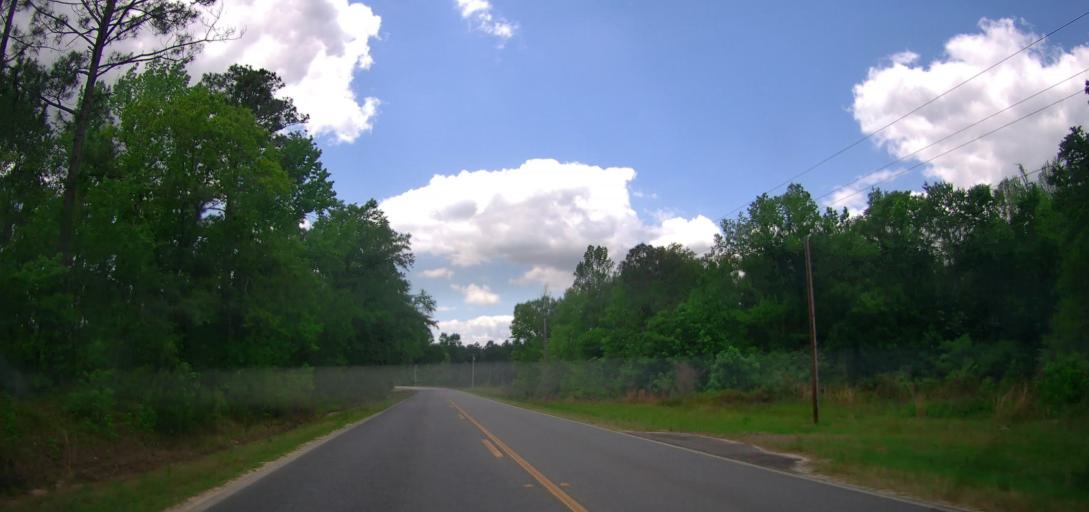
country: US
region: Georgia
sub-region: Laurens County
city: East Dublin
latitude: 32.5254
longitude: -82.7533
